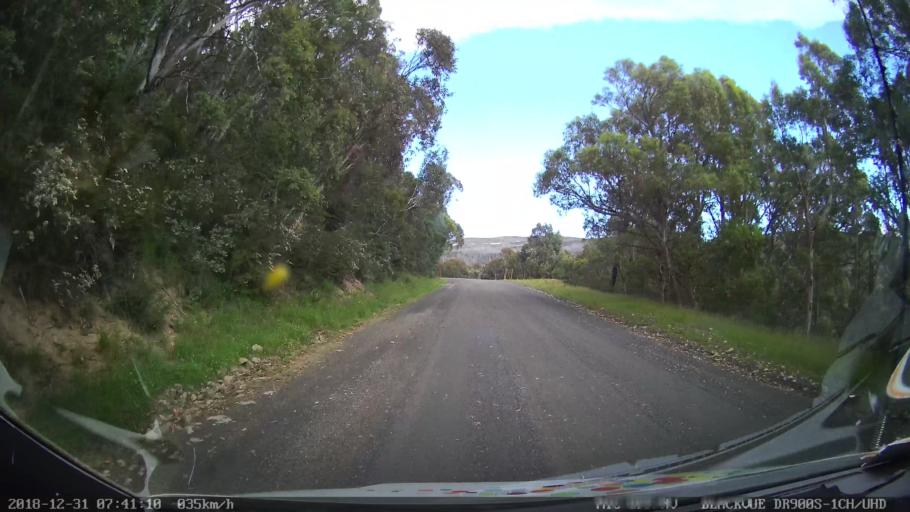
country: AU
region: New South Wales
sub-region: Snowy River
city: Jindabyne
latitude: -36.3529
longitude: 148.4136
